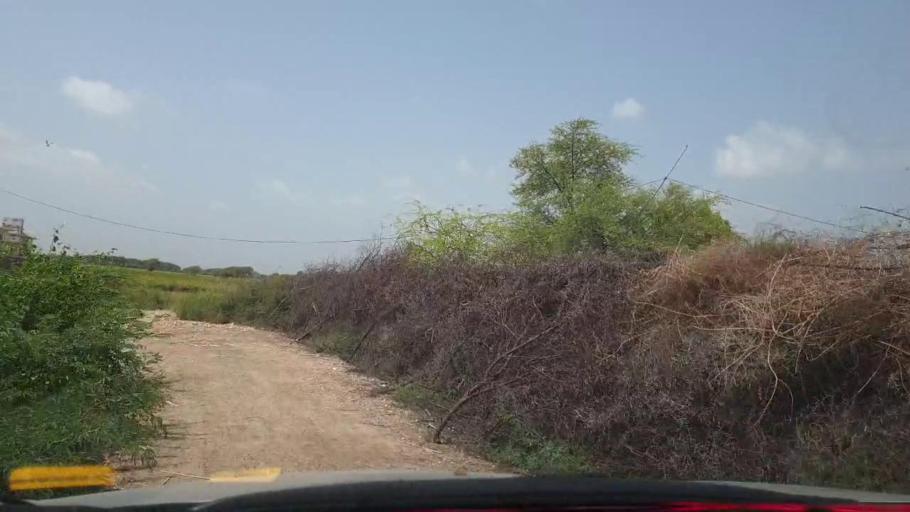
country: PK
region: Sindh
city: Rajo Khanani
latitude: 24.9323
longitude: 68.8985
